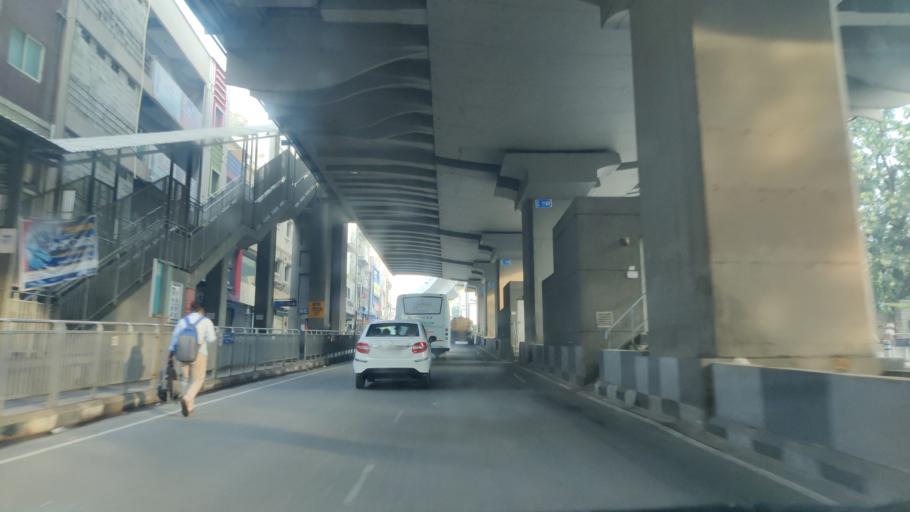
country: IN
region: Telangana
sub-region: Hyderabad
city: Malkajgiri
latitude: 17.4358
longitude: 78.5054
